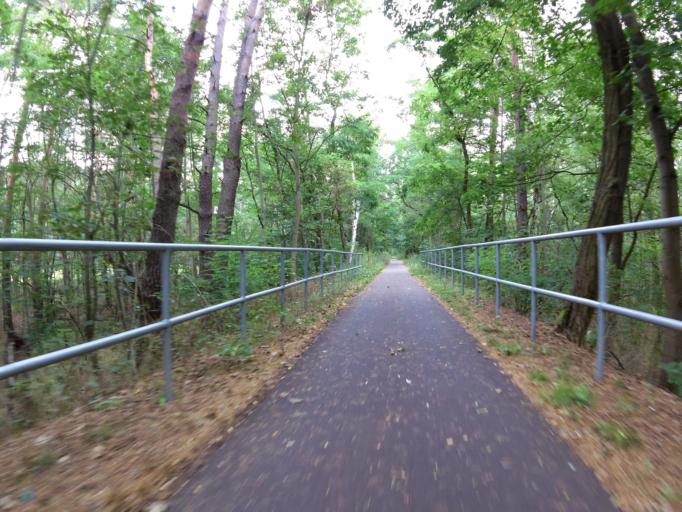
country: DE
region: Brandenburg
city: Diensdorf-Radlow
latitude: 52.2524
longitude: 14.0396
